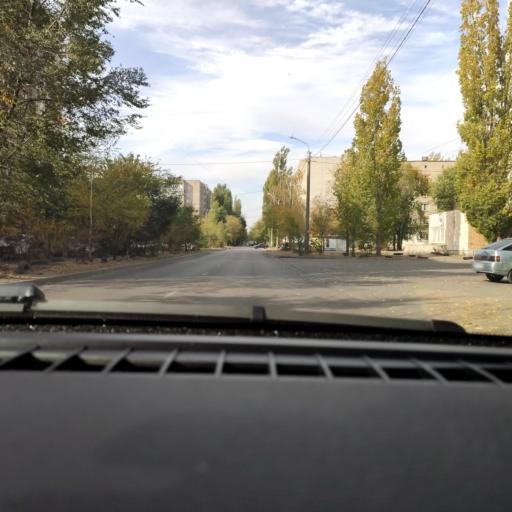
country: RU
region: Voronezj
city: Maslovka
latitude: 51.6330
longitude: 39.2836
